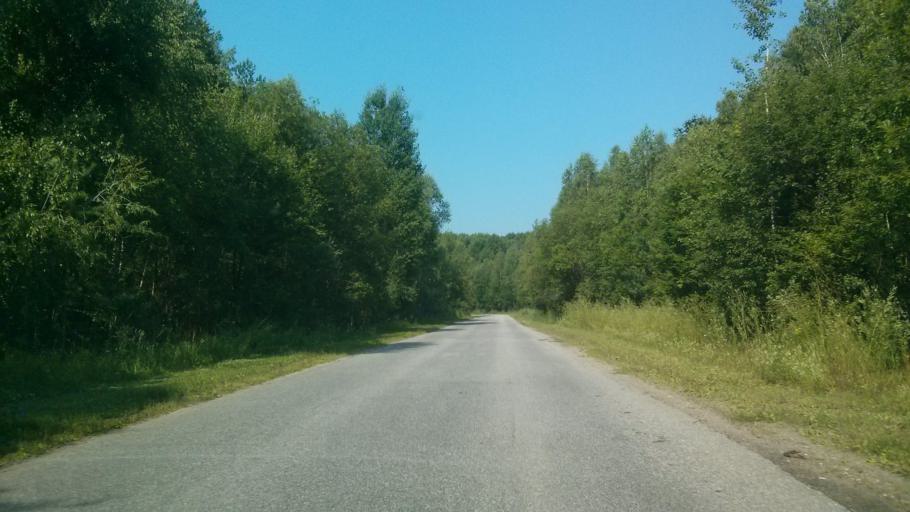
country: RU
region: Vladimir
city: Murom
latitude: 55.5063
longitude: 41.9940
